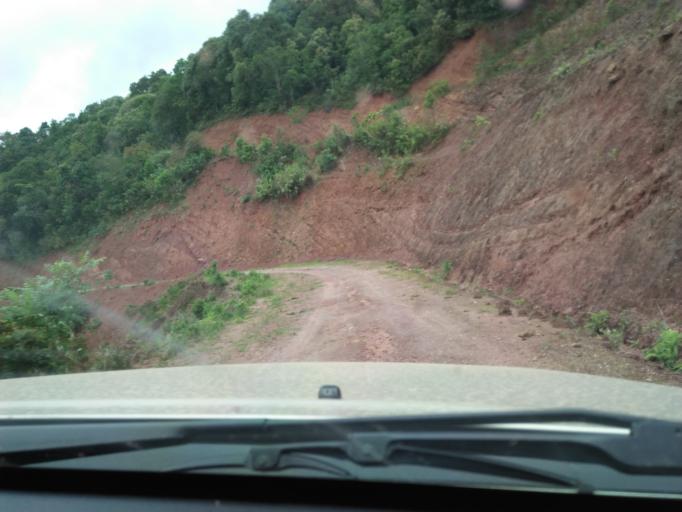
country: TH
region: Nan
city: Bo Kluea
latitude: 19.3754
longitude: 101.2159
